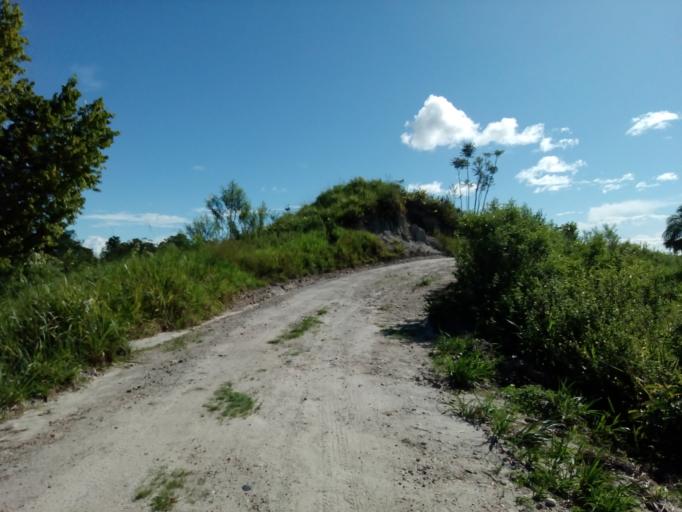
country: CO
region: Boyaca
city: Puerto Boyaca
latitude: 6.0011
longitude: -74.3720
